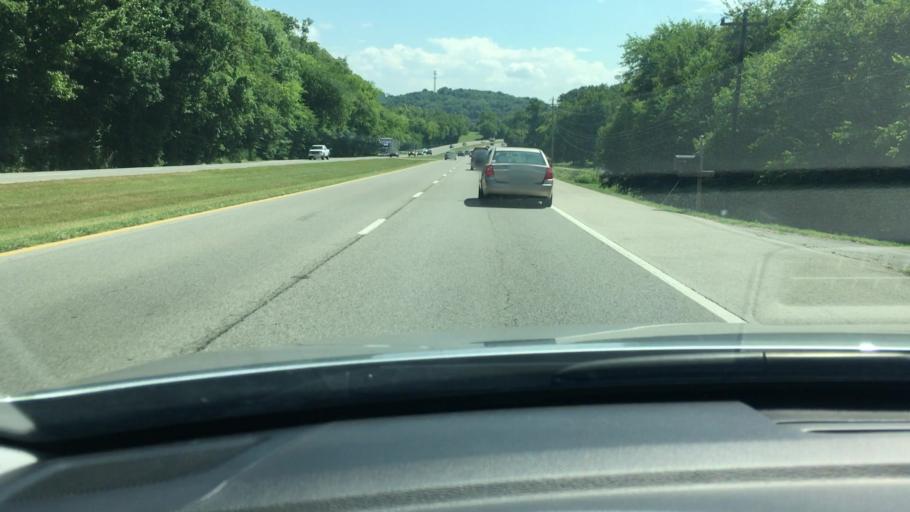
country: US
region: Tennessee
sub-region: Maury County
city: Columbia
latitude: 35.6795
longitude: -86.9988
